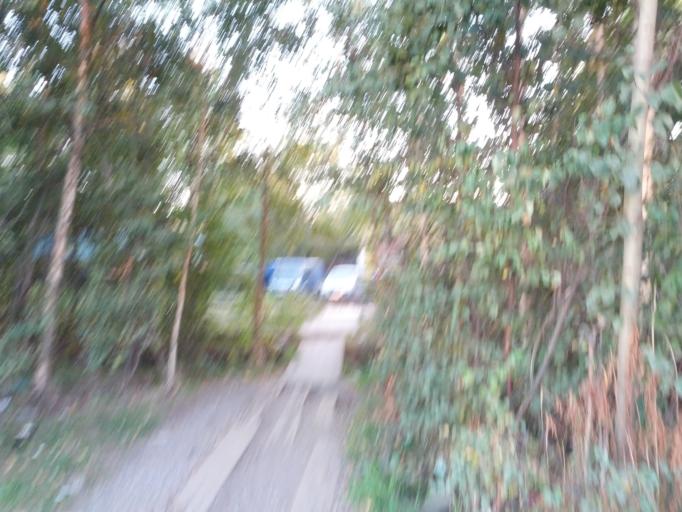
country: RU
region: St.-Petersburg
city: Obukhovo
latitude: 59.9119
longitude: 30.4395
